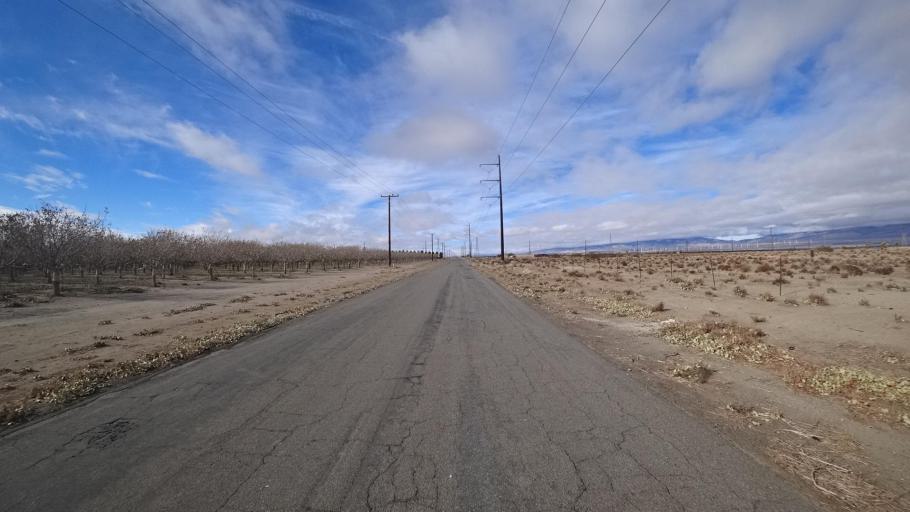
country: US
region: California
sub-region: Kern County
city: Rosamond
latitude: 34.8344
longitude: -118.3223
